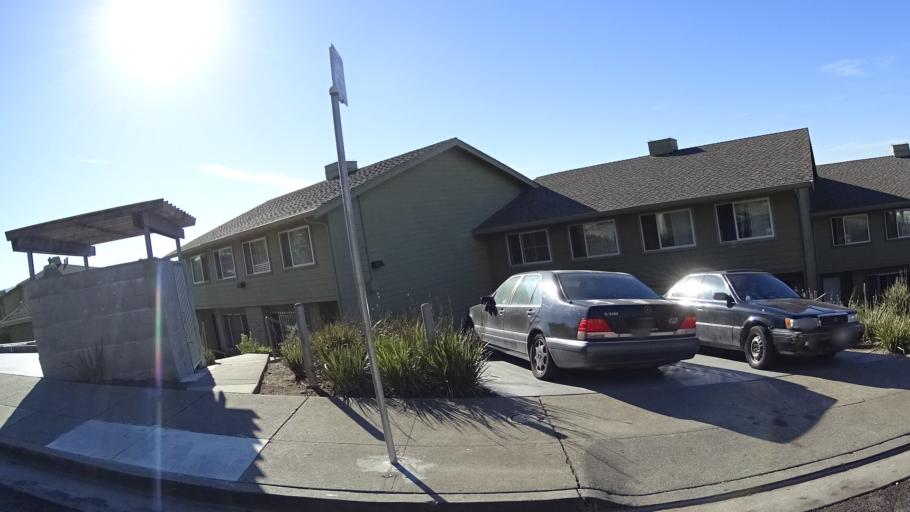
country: US
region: California
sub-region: San Francisco County
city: San Francisco
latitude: 37.7370
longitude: -122.3867
